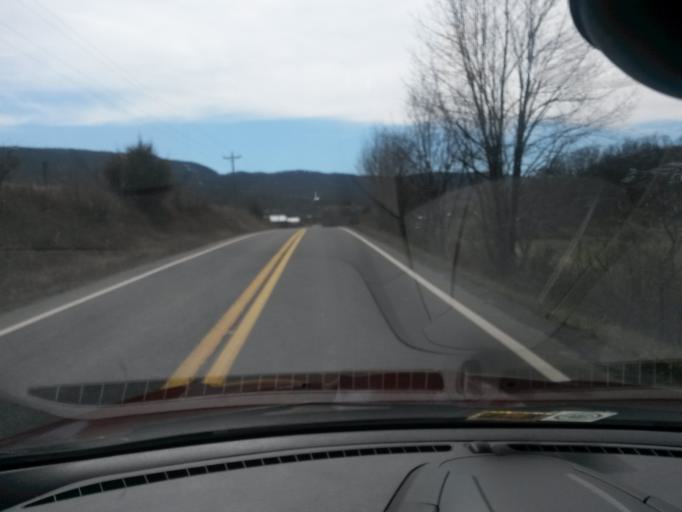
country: US
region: West Virginia
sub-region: Greenbrier County
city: White Sulphur Springs
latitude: 37.6369
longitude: -80.2395
